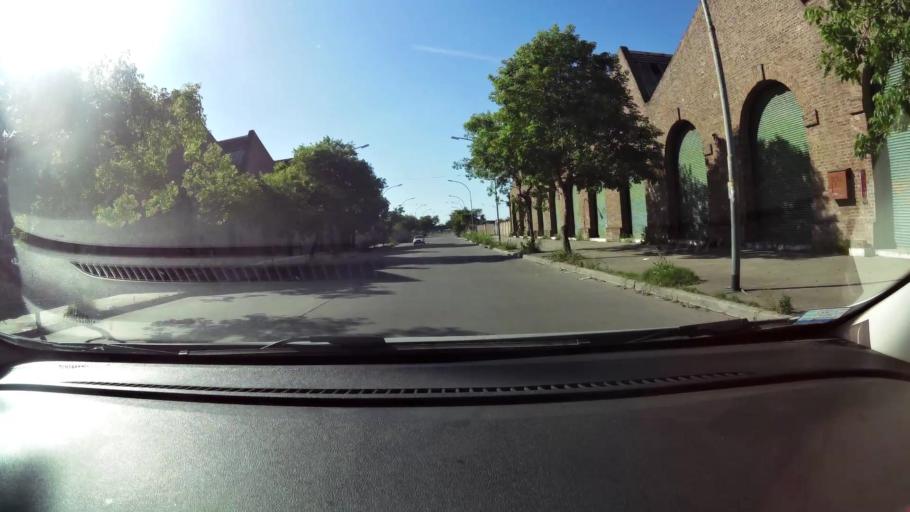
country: AR
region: Cordoba
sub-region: Departamento de Capital
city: Cordoba
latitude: -31.3958
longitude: -64.1630
